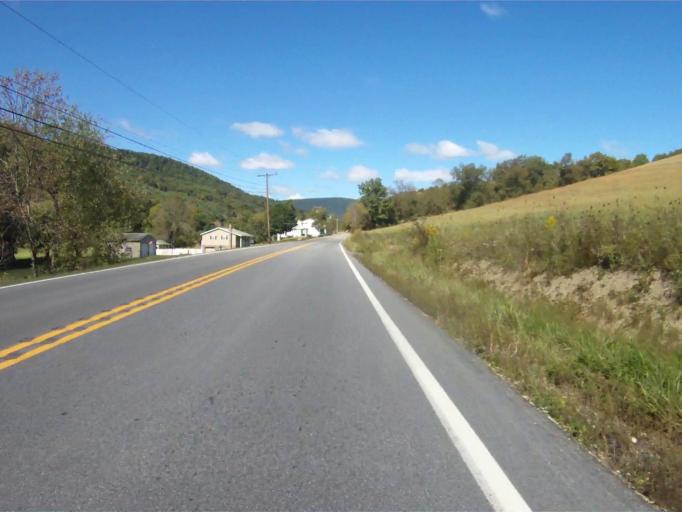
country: US
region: Pennsylvania
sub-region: Centre County
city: Houserville
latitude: 40.9108
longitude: -77.8839
